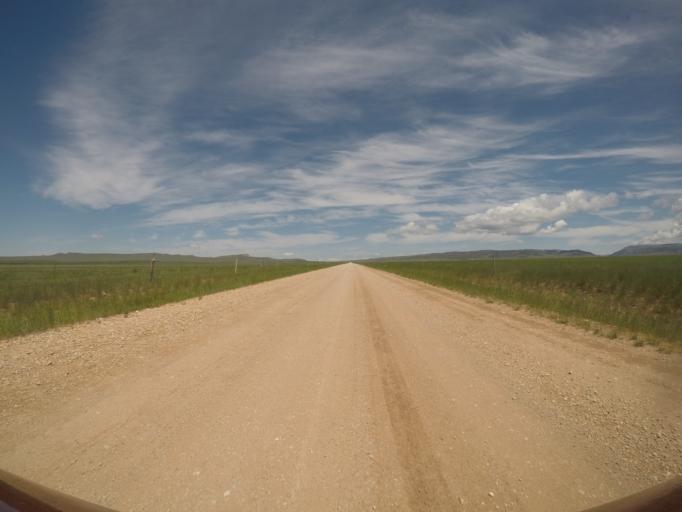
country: US
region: Wyoming
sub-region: Park County
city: Powell
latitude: 45.2094
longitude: -108.7191
